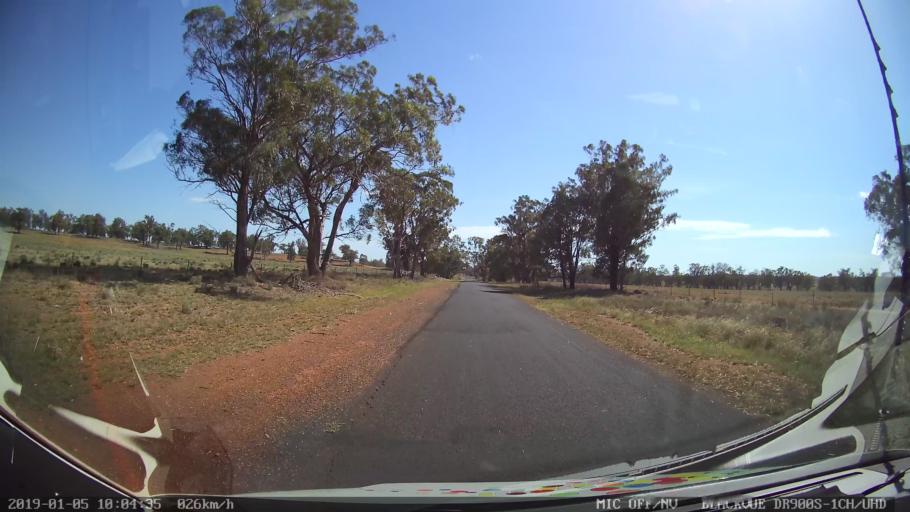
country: AU
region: New South Wales
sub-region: Gilgandra
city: Gilgandra
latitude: -31.6728
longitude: 148.8610
